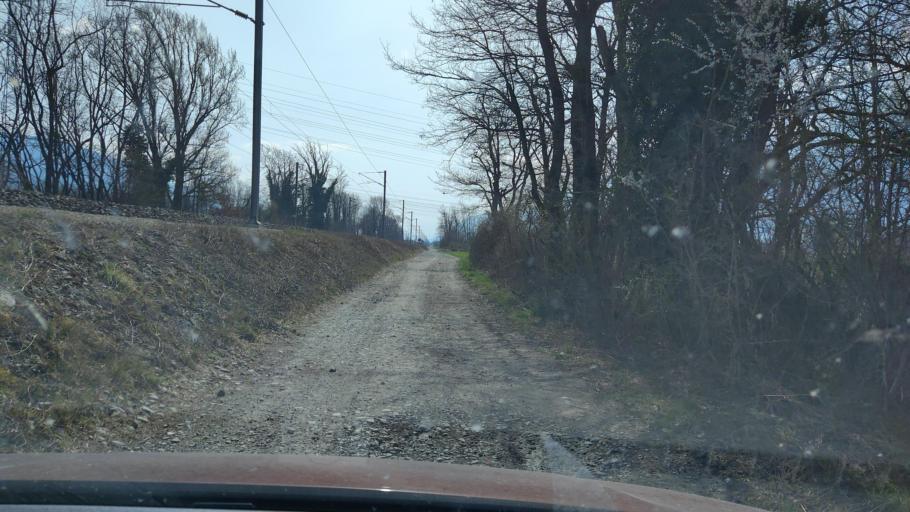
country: FR
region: Rhone-Alpes
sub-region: Departement de la Savoie
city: Montmelian
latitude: 45.4714
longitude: 6.0356
